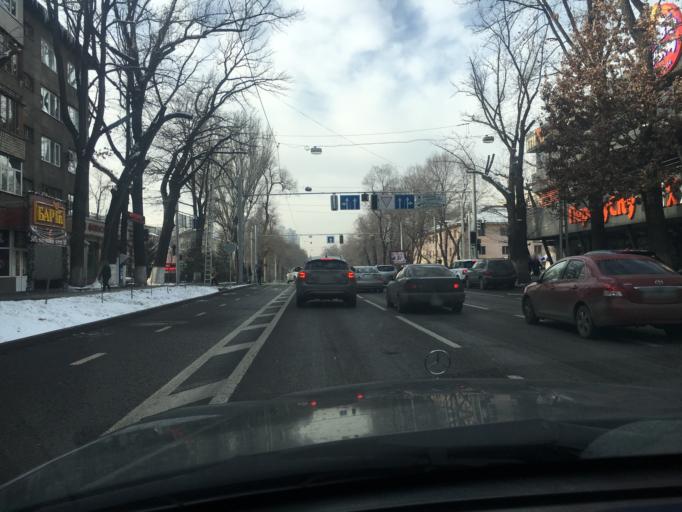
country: KZ
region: Almaty Qalasy
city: Almaty
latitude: 43.2450
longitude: 76.9278
